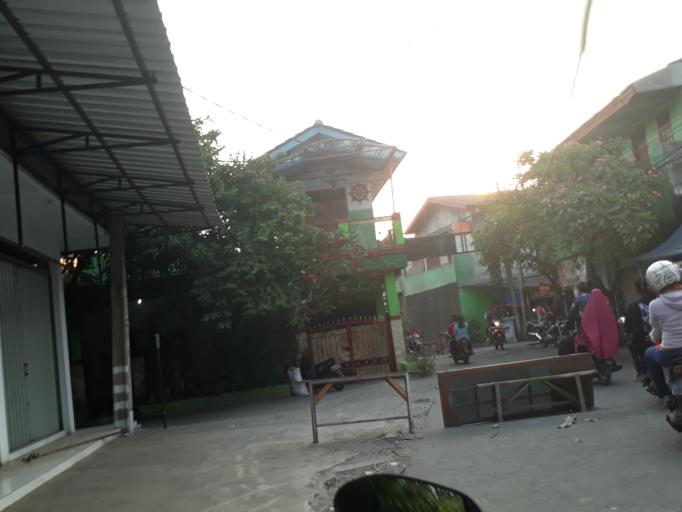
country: ID
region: West Java
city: Bekasi
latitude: -6.2432
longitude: 107.0517
